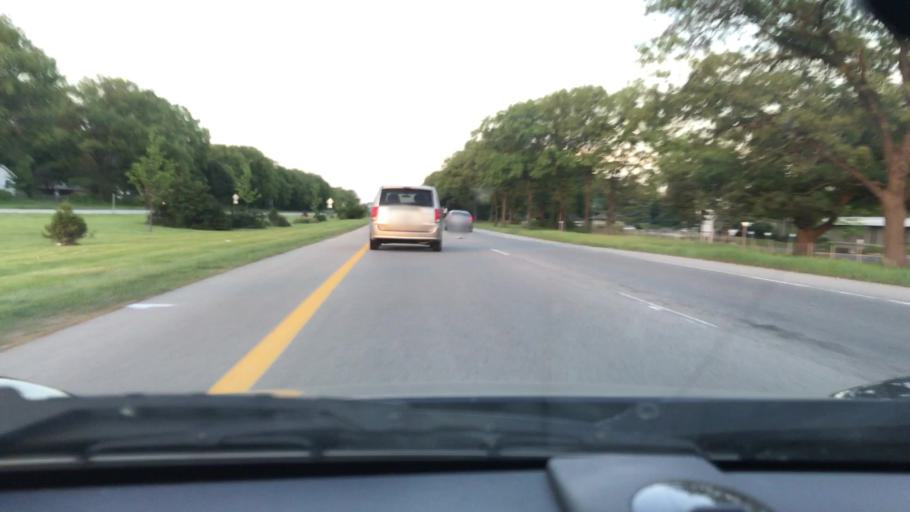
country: US
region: Michigan
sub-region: Muskegon County
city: Roosevelt Park
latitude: 43.1894
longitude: -86.2570
